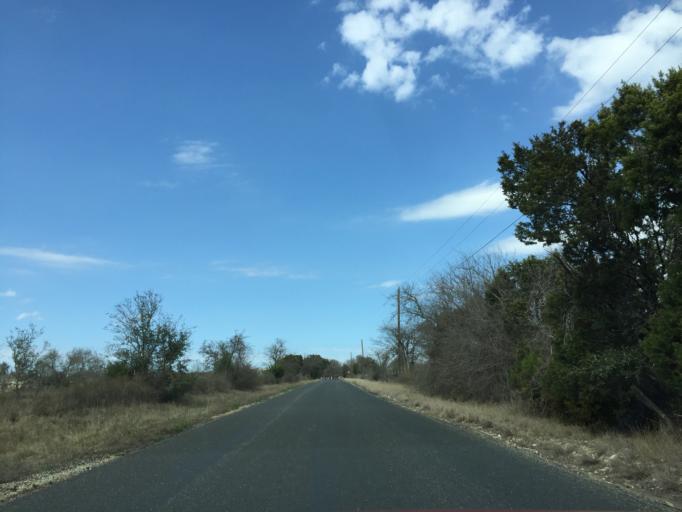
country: US
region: Texas
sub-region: Burnet County
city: Bertram
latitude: 30.7448
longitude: -97.9395
